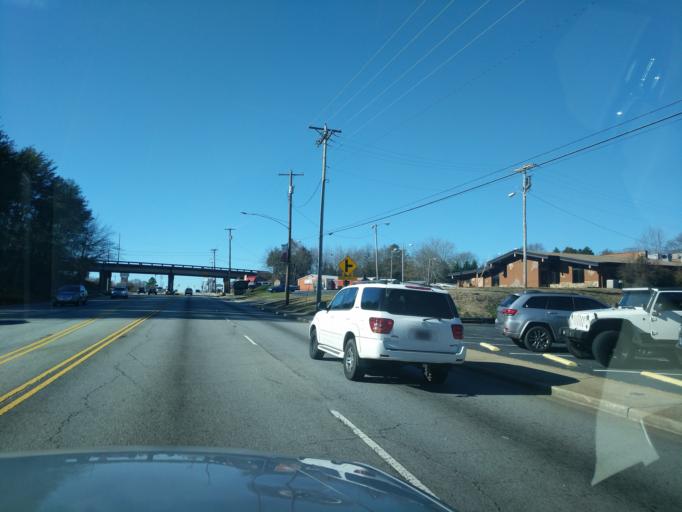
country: US
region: South Carolina
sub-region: Pickens County
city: Easley
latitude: 34.8231
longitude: -82.5815
